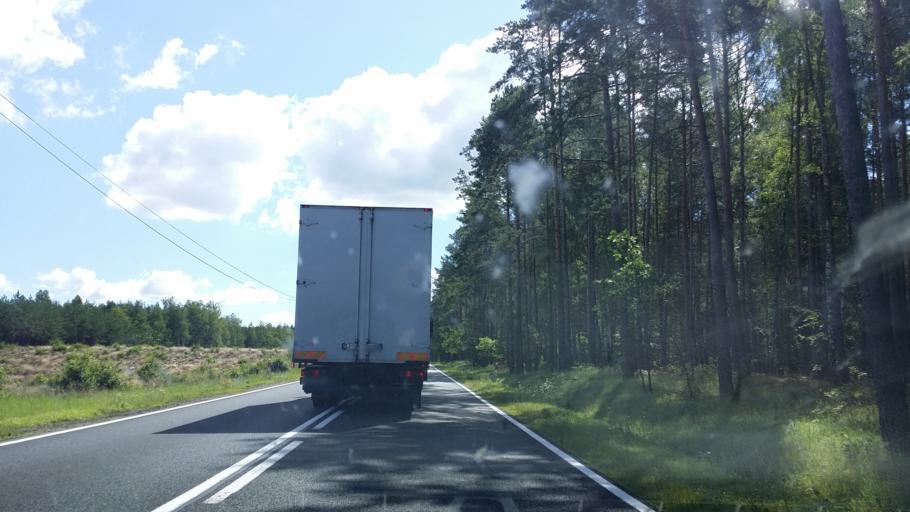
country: PL
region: West Pomeranian Voivodeship
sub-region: Powiat choszczenski
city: Drawno
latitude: 53.3017
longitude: 15.7969
